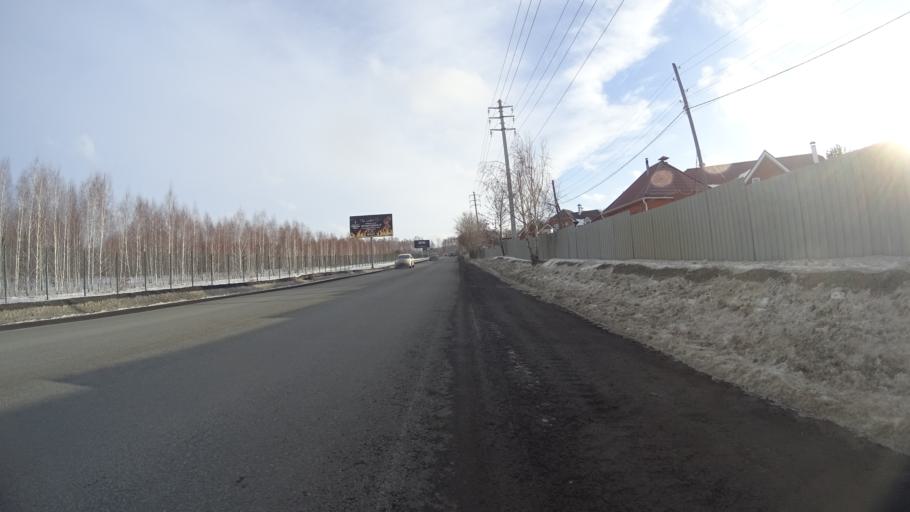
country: RU
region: Chelyabinsk
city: Sargazy
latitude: 55.1320
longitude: 61.2868
